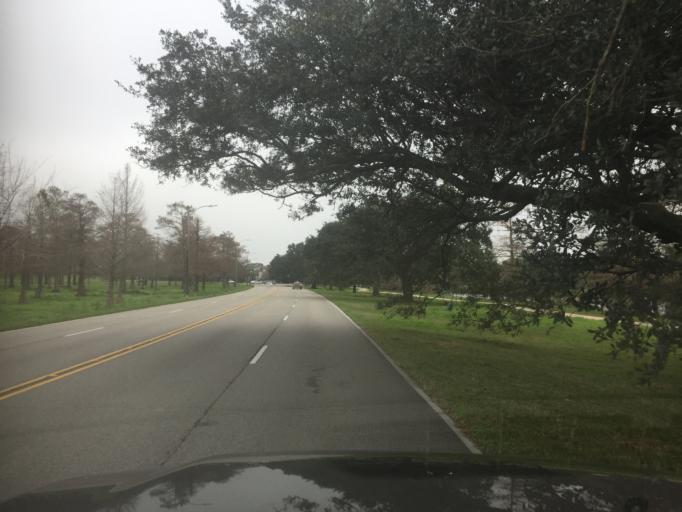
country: US
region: Louisiana
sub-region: Jefferson Parish
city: Metairie
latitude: 30.0164
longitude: -90.0970
